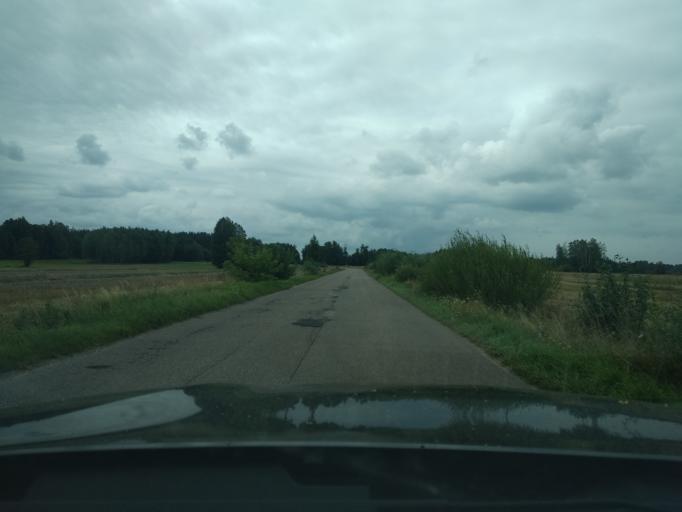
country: PL
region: Masovian Voivodeship
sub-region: Powiat pultuski
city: Obryte
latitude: 52.7466
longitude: 21.2154
